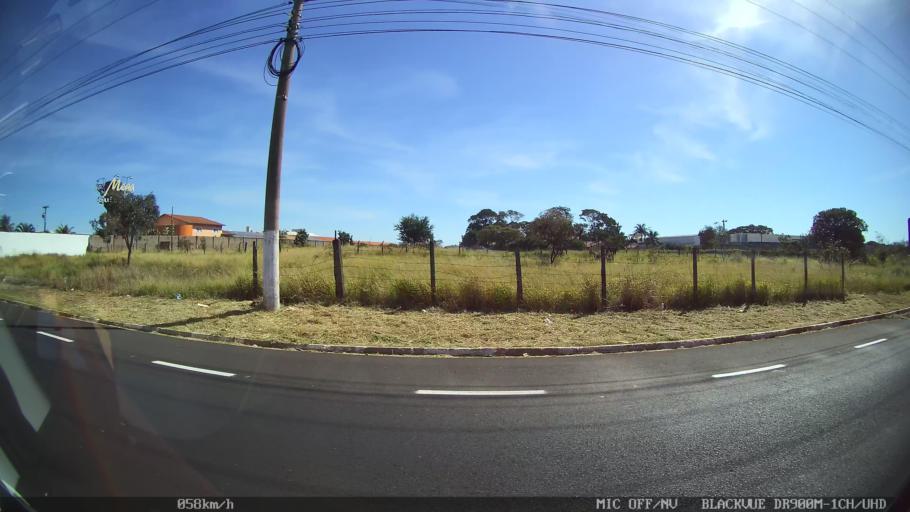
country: BR
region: Sao Paulo
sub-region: Franca
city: Franca
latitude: -20.5477
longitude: -47.4266
